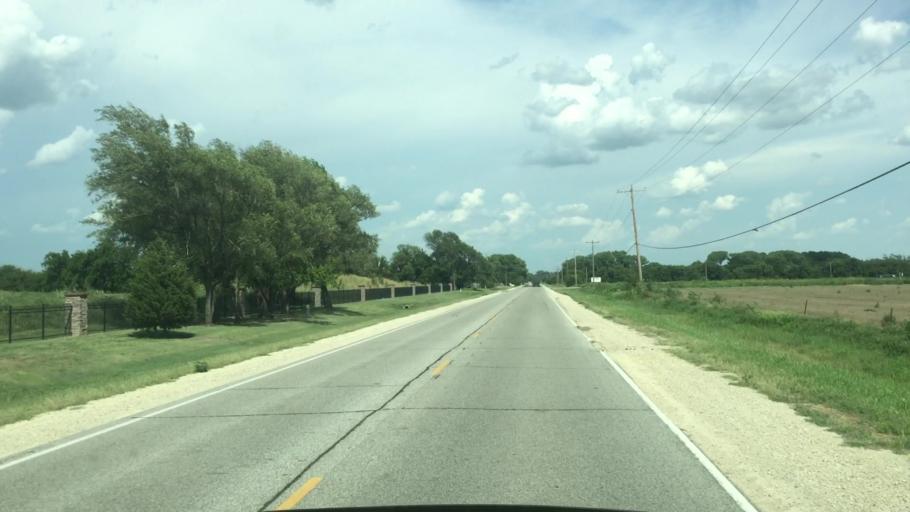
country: US
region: Kansas
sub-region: Sedgwick County
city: Maize
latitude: 37.7810
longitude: -97.4422
